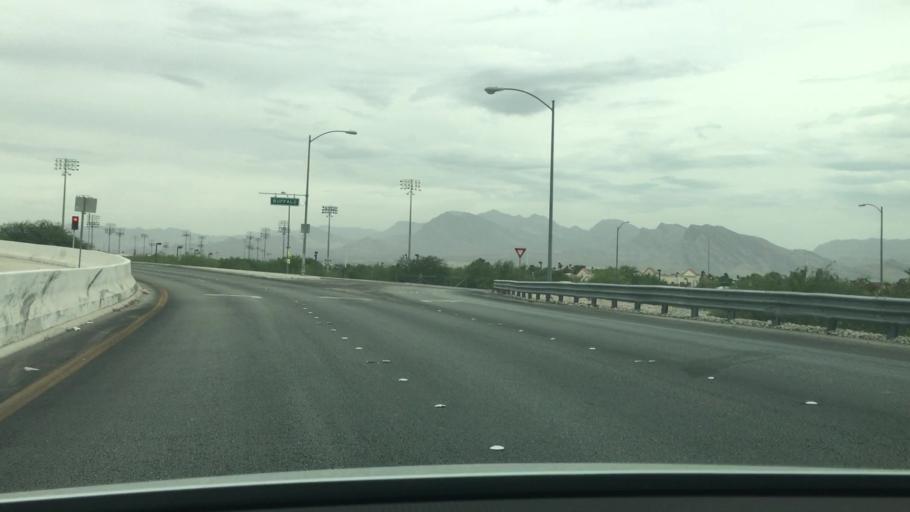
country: US
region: Nevada
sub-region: Clark County
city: Spring Valley
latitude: 36.1800
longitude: -115.2591
